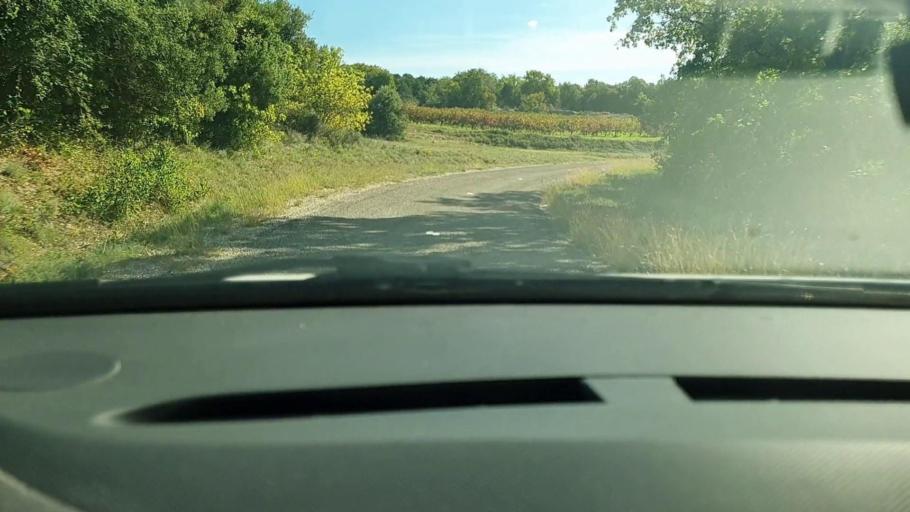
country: FR
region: Languedoc-Roussillon
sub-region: Departement du Gard
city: Barjac
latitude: 44.1948
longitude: 4.3155
